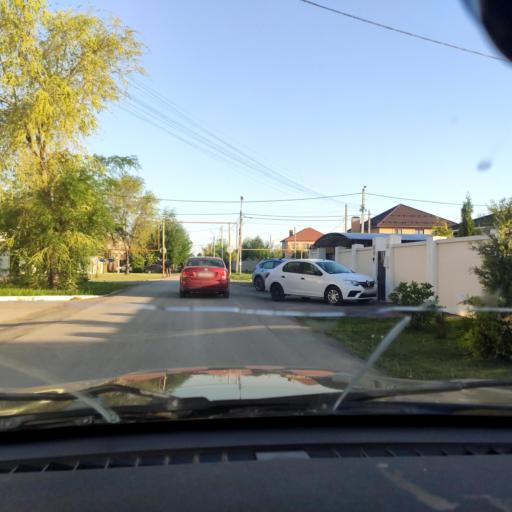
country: RU
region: Samara
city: Podstepki
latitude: 53.5127
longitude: 49.1678
